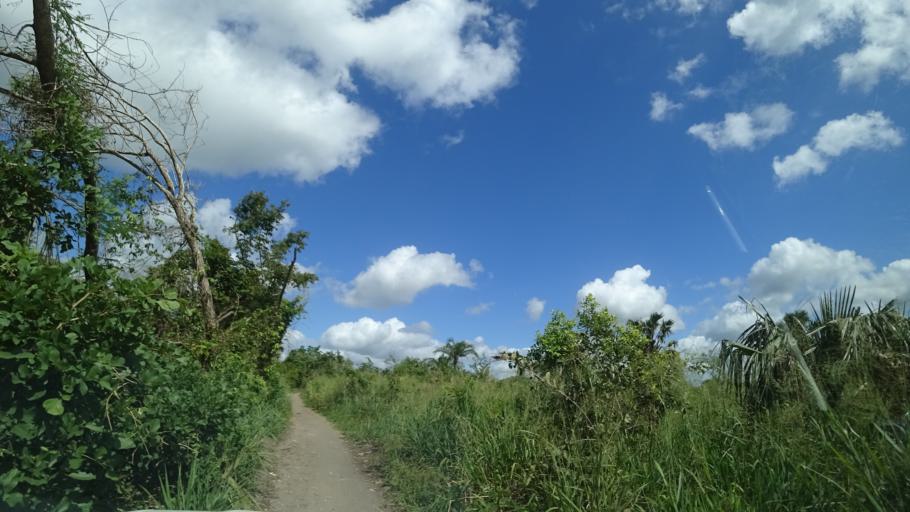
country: MZ
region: Sofala
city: Dondo
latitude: -19.3593
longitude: 34.5770
